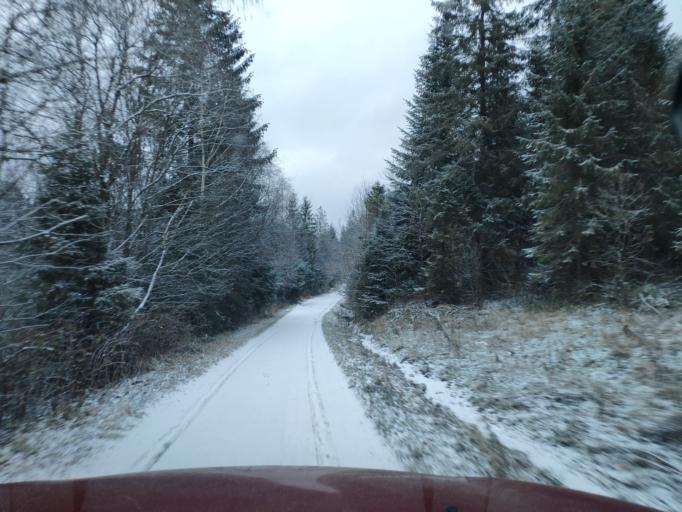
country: SK
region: Kosicky
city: Spisska Nova Ves
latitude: 48.8152
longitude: 20.5379
